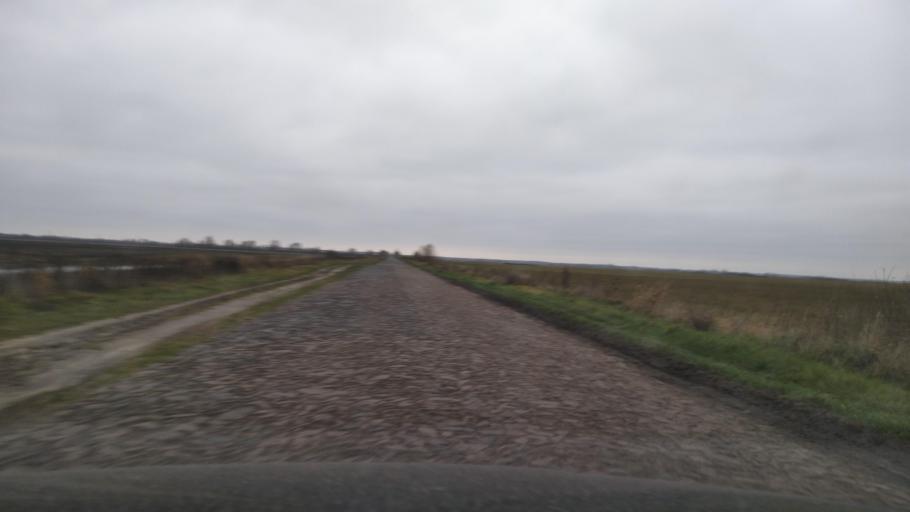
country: BY
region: Brest
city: Davyd-Haradok
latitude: 52.0112
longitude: 27.2056
